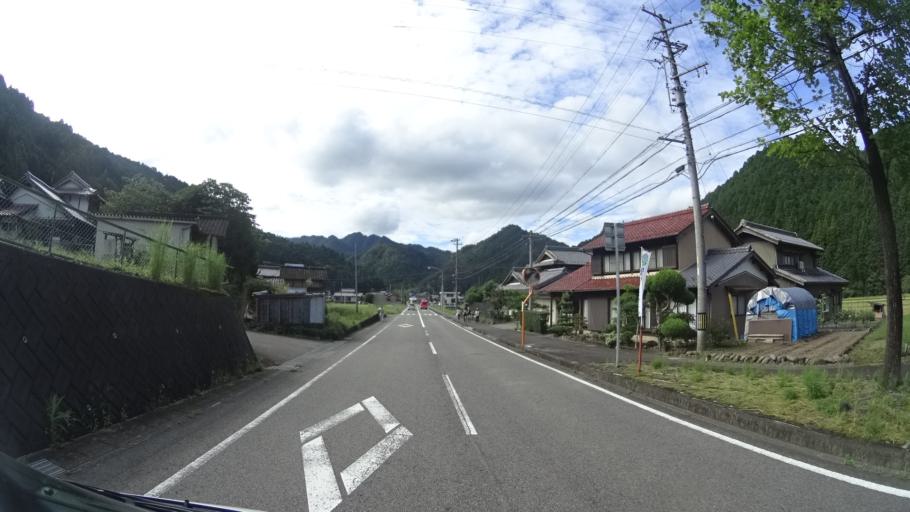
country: JP
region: Gifu
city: Minokamo
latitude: 35.5711
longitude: 137.0846
